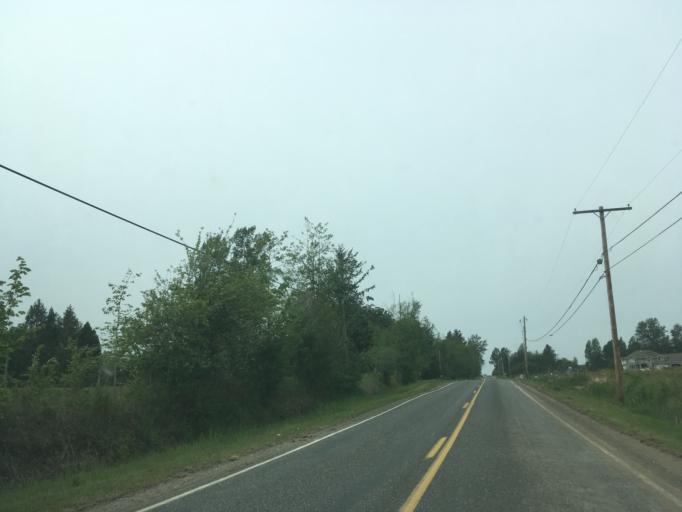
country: US
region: Washington
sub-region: Whatcom County
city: Bellingham
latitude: 48.8188
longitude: -122.4598
